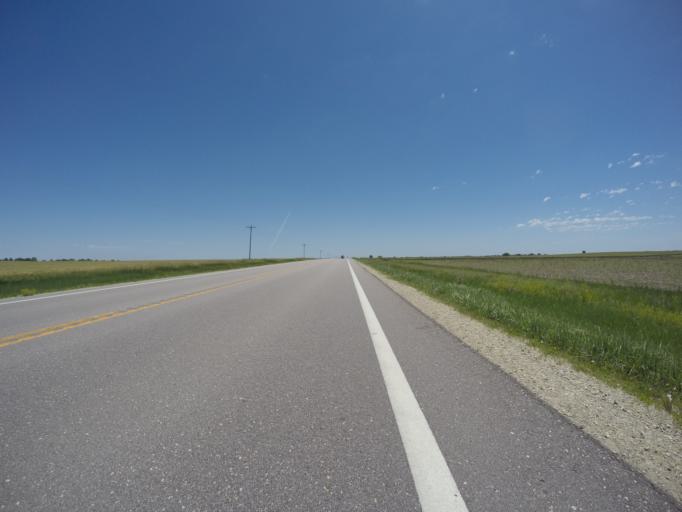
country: US
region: Kansas
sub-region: Republic County
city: Belleville
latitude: 39.8127
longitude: -97.6817
